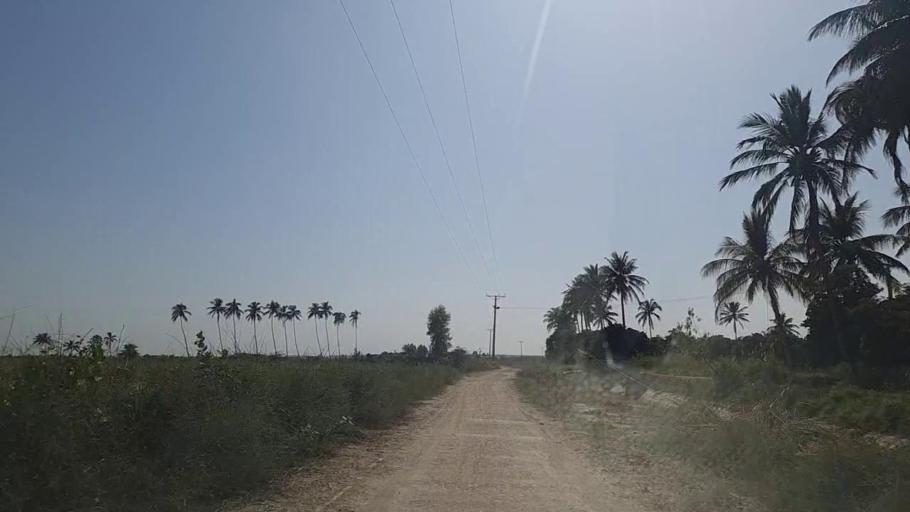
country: PK
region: Sindh
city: Thatta
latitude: 24.6354
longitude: 67.8856
